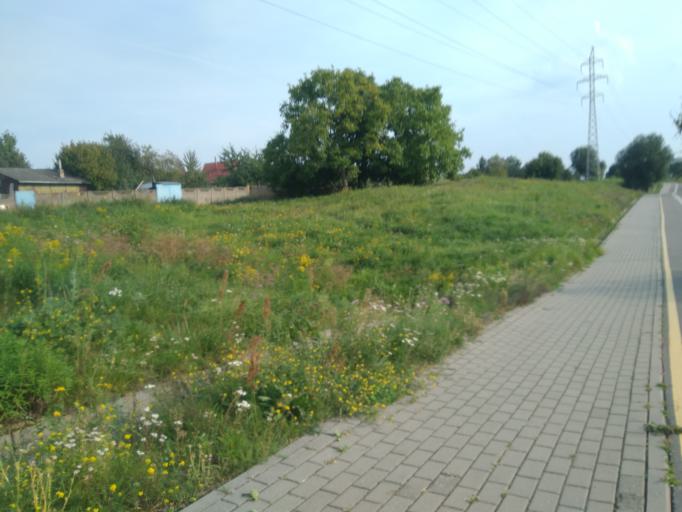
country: BY
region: Minsk
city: Minsk
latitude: 53.8458
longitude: 27.5987
